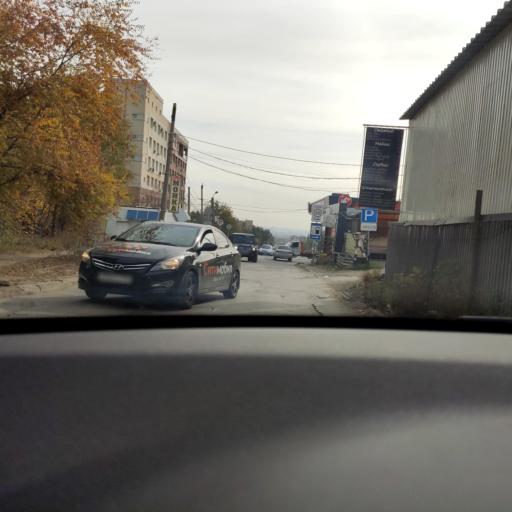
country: RU
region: Samara
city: Samara
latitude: 53.2184
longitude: 50.2205
